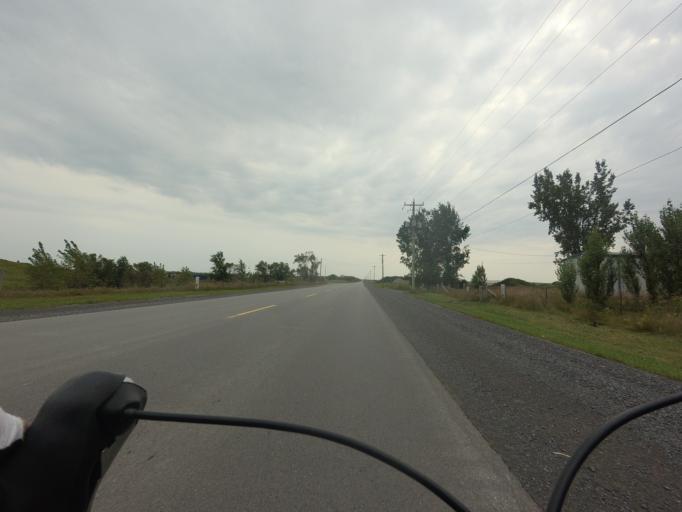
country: CA
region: Ontario
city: Bells Corners
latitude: 45.2282
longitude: -75.7788
